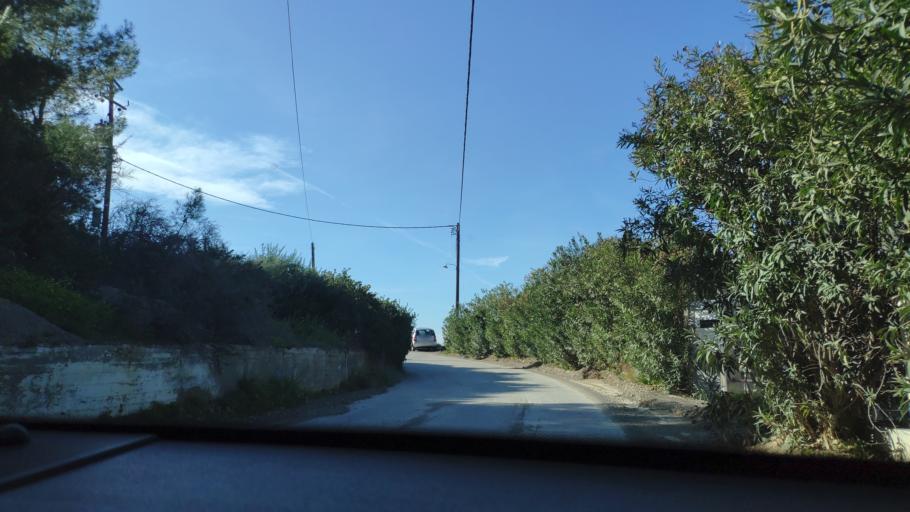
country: GR
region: Peloponnese
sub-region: Nomos Korinthias
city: Agioi Theodoroi
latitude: 38.0596
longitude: 23.0987
